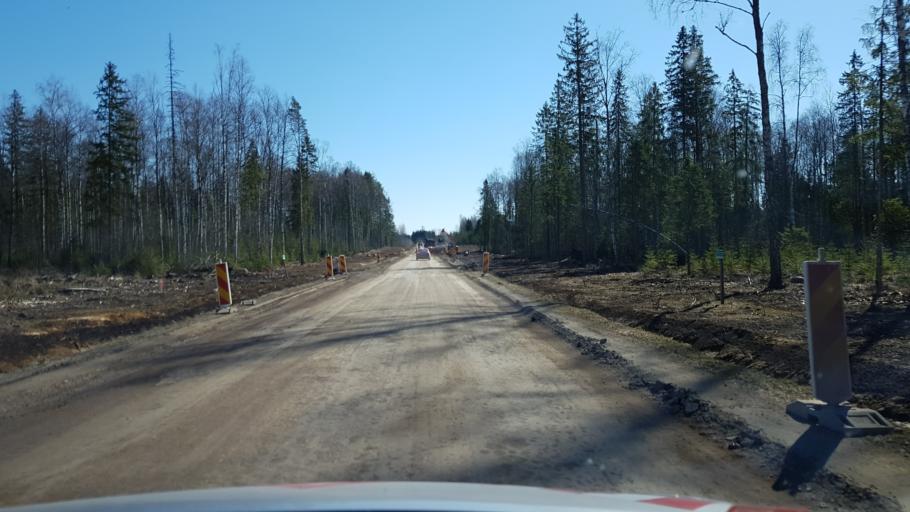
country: EE
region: Jogevamaa
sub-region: Mustvee linn
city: Mustvee
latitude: 59.0398
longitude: 26.6712
